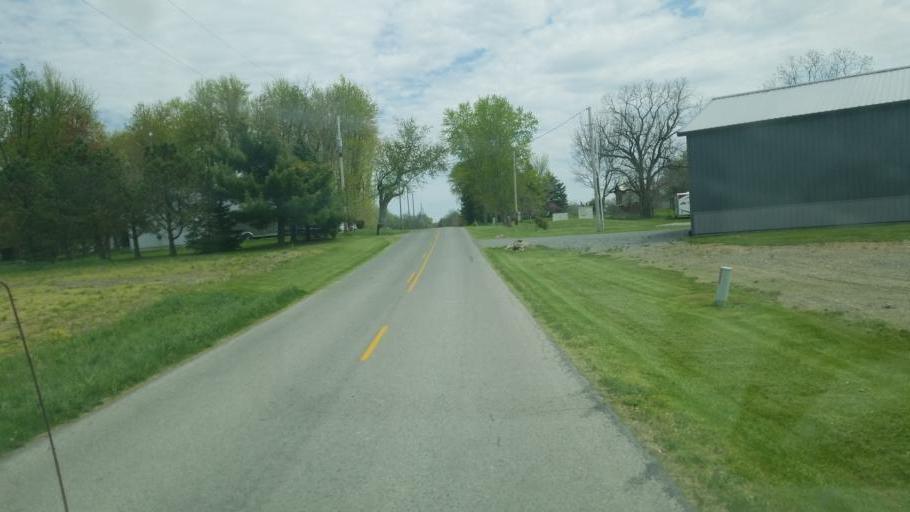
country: US
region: Ohio
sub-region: Allen County
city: Bluffton
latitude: 40.7835
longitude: -83.9718
